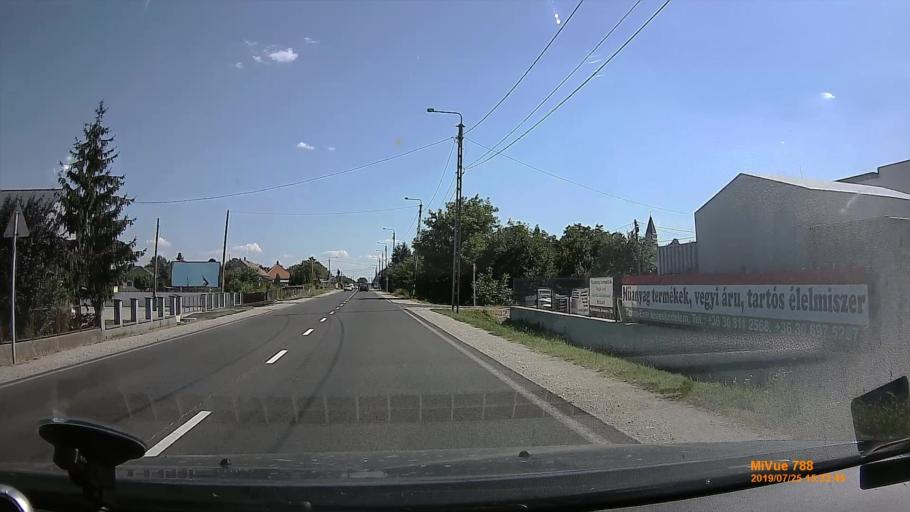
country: HU
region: Borsod-Abauj-Zemplen
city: Nyekladhaza
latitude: 47.9924
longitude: 20.8302
